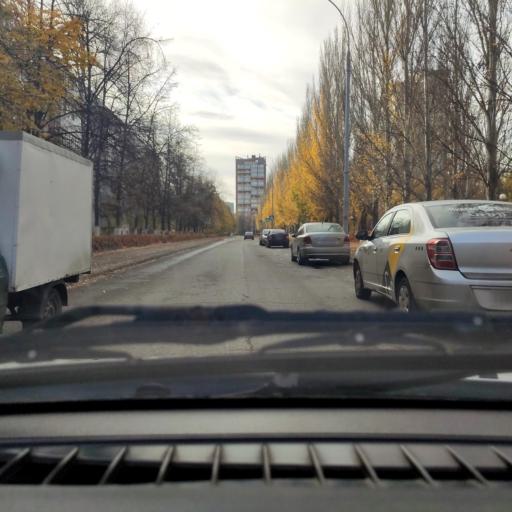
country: RU
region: Samara
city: Tol'yatti
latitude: 53.5296
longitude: 49.3042
